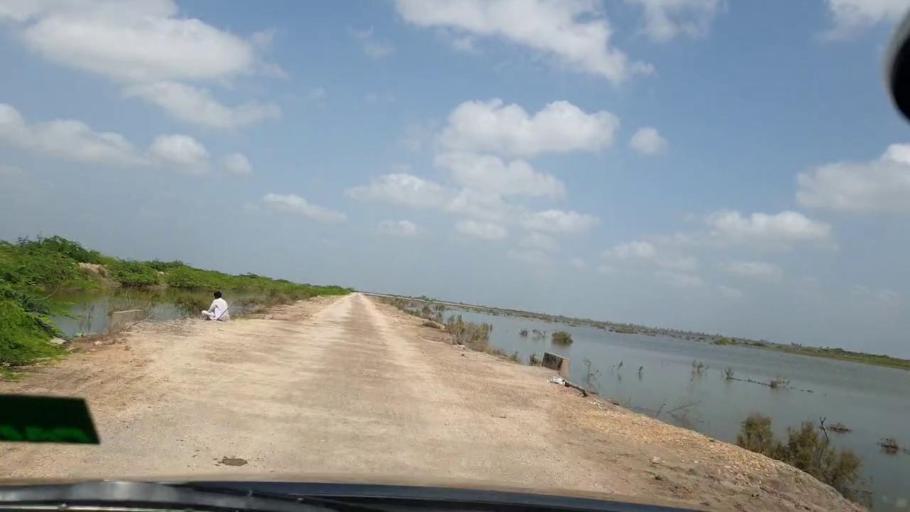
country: PK
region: Sindh
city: Kadhan
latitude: 24.5779
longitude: 69.1427
